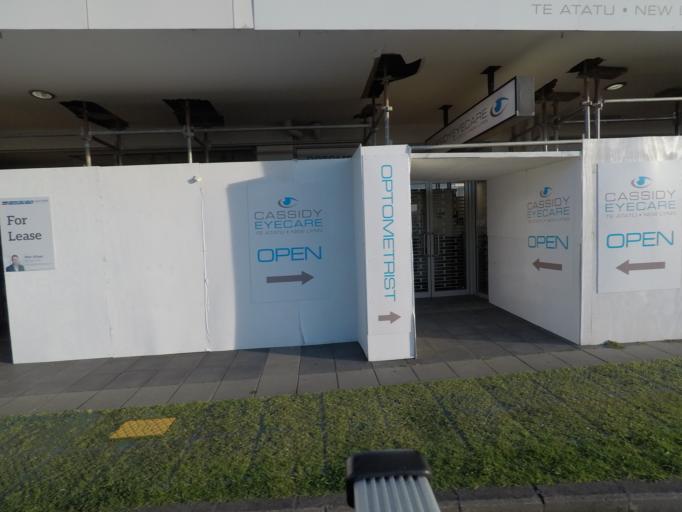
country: NZ
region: Auckland
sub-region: Auckland
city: Rosebank
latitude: -36.8436
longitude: 174.6519
